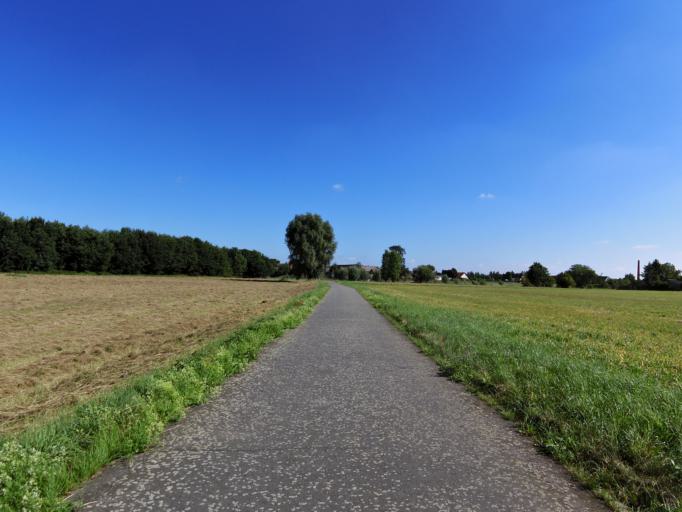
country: DE
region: Saxony
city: Strehla
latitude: 51.3692
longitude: 13.2508
